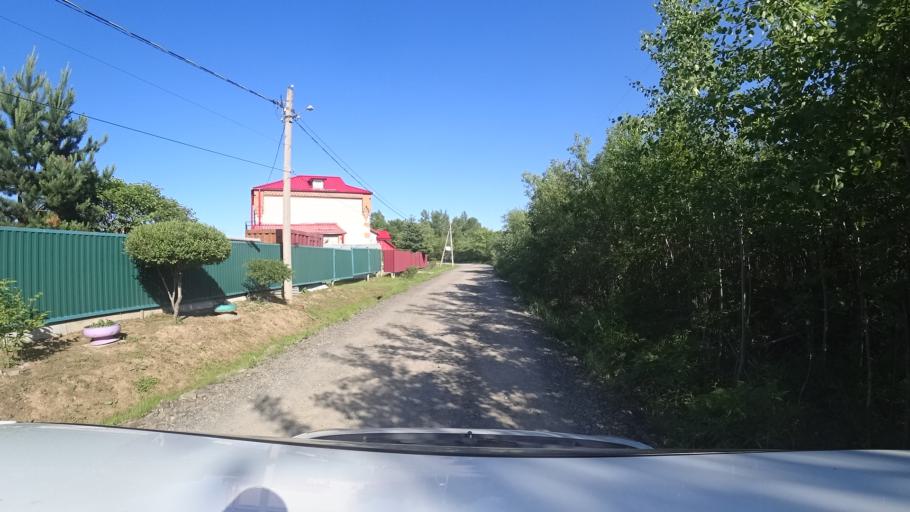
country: RU
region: Khabarovsk Krai
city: Topolevo
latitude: 48.5412
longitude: 135.1722
